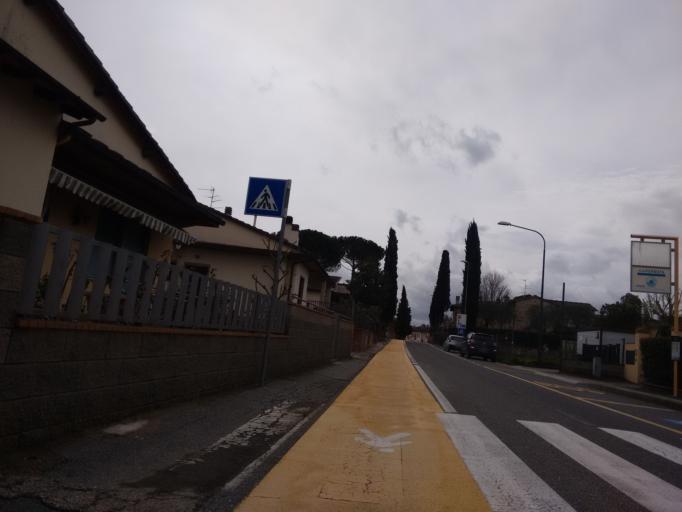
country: IT
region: Tuscany
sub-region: Province of Florence
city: Strada in Chianti
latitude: 43.6622
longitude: 11.2946
